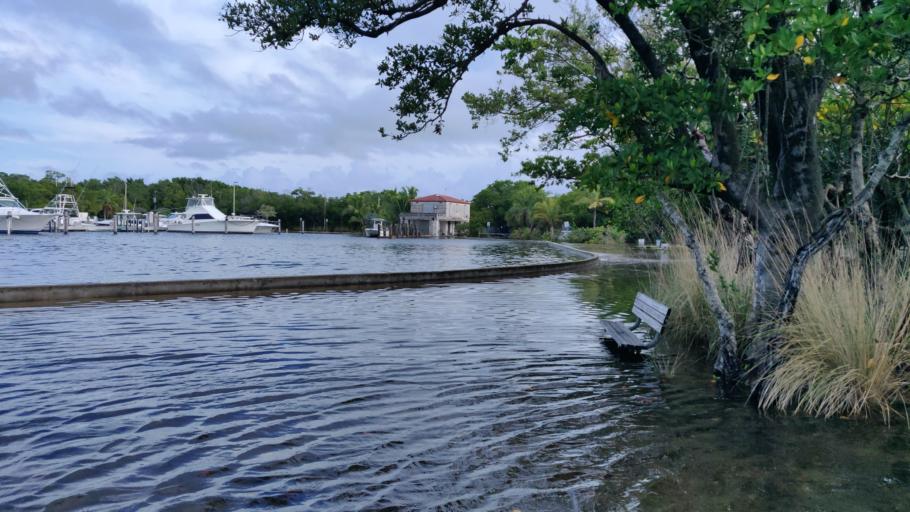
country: US
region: Florida
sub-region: Miami-Dade County
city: Coconut Grove
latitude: 25.6785
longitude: -80.2580
